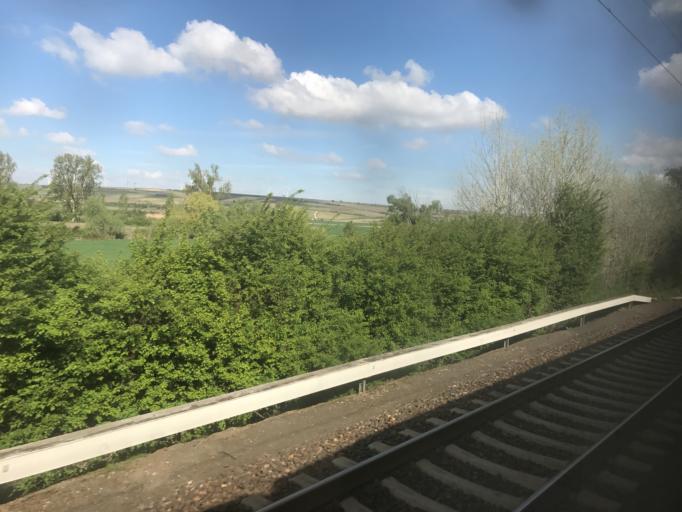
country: DE
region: Rheinland-Pfalz
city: Osthofen
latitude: 49.7210
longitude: 8.3280
